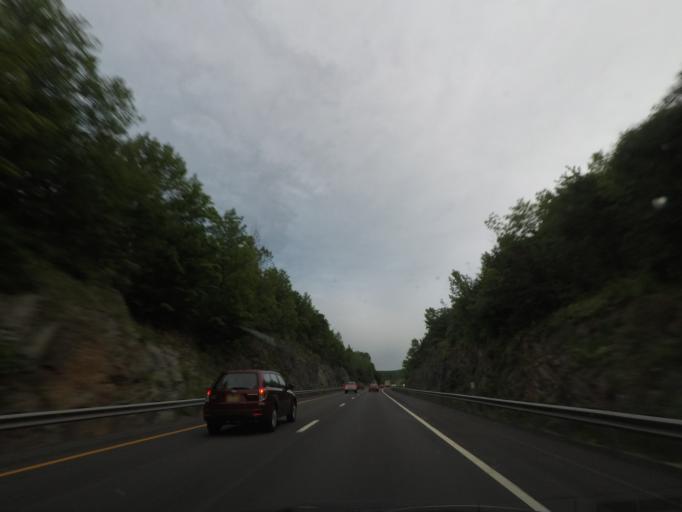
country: US
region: New York
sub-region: Columbia County
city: Chatham
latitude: 42.4309
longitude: -73.5531
